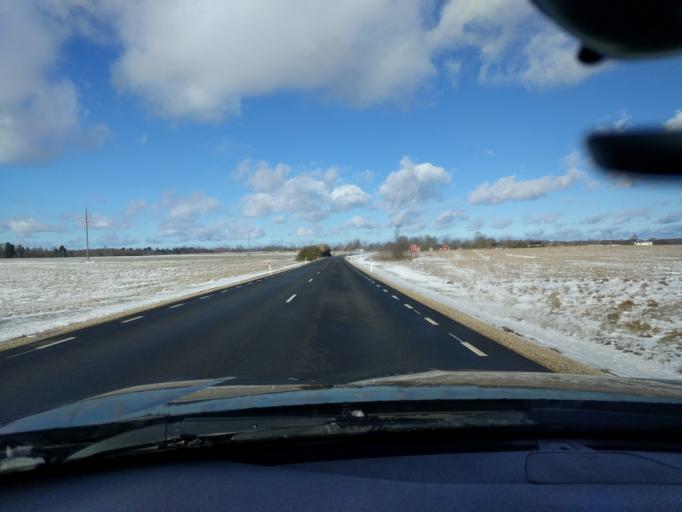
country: EE
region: Harju
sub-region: Raasiku vald
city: Raasiku
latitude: 59.2939
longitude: 25.1795
